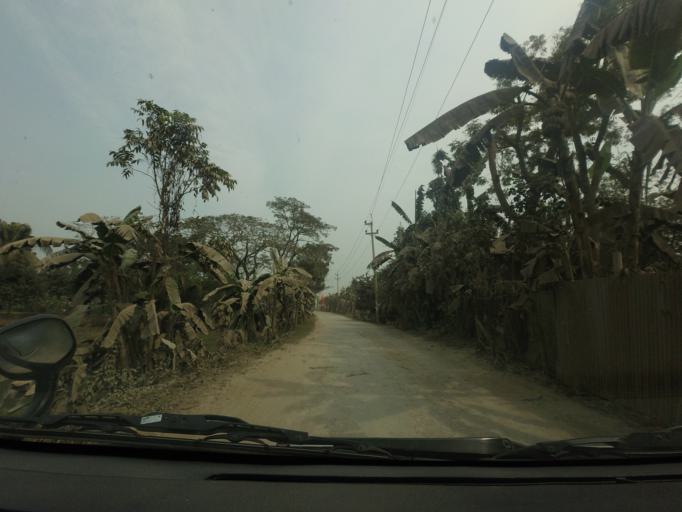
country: BD
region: Dhaka
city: Kishorganj
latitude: 24.3445
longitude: 90.7656
